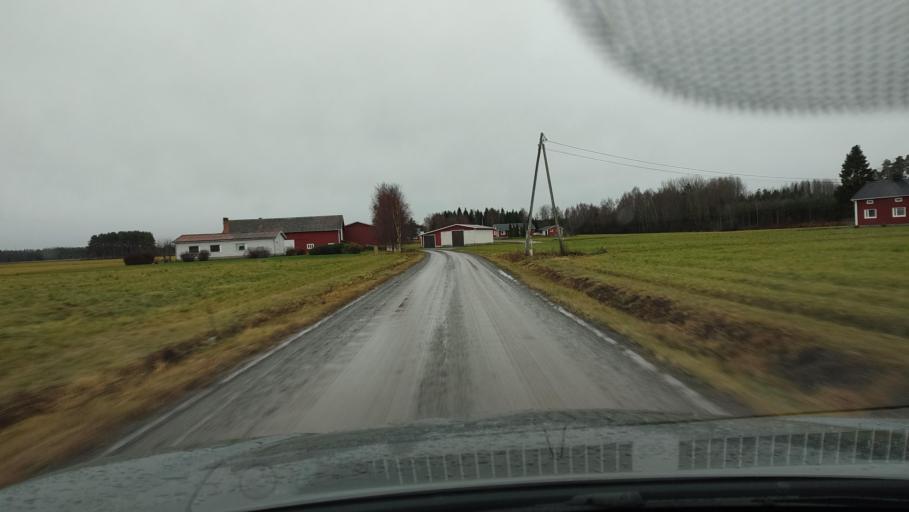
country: FI
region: Southern Ostrobothnia
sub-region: Suupohja
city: Karijoki
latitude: 62.2398
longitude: 21.5512
